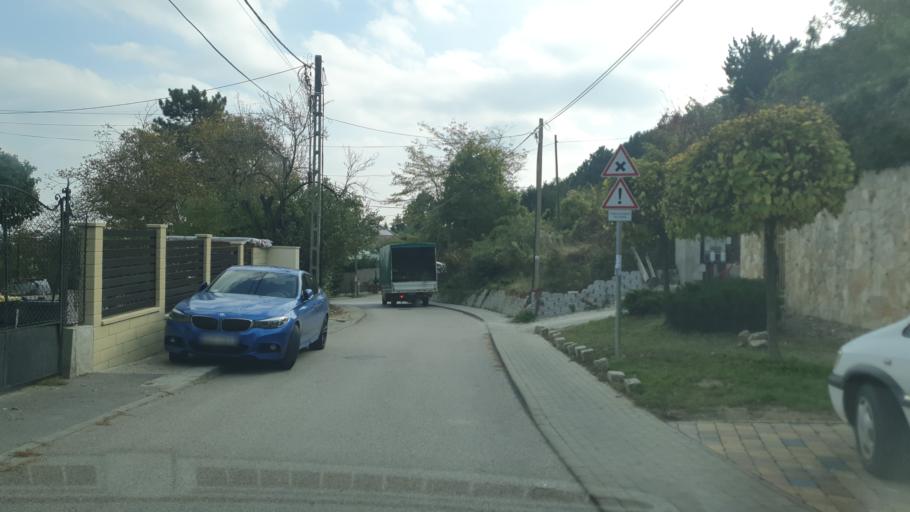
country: HU
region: Budapest
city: Budapest III. keruelet
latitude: 47.5447
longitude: 19.0176
